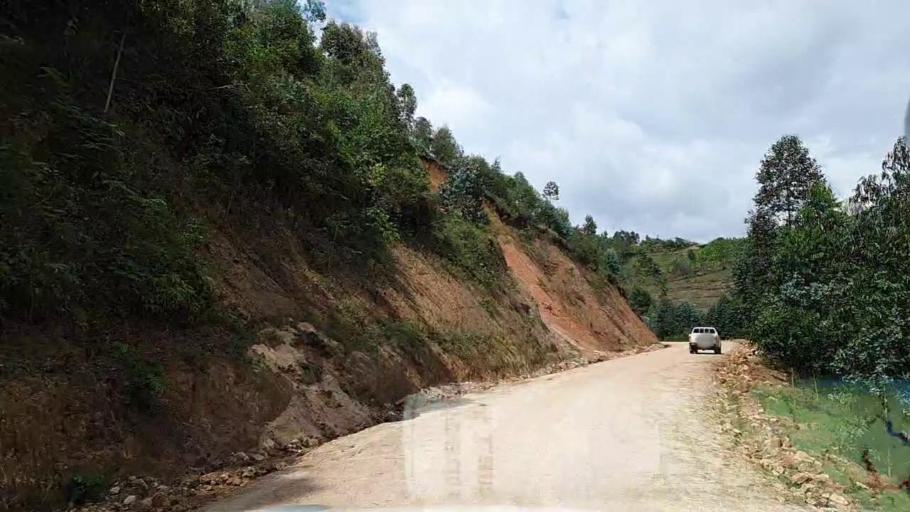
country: RW
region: Southern Province
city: Nzega
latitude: -2.3353
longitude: 29.4416
